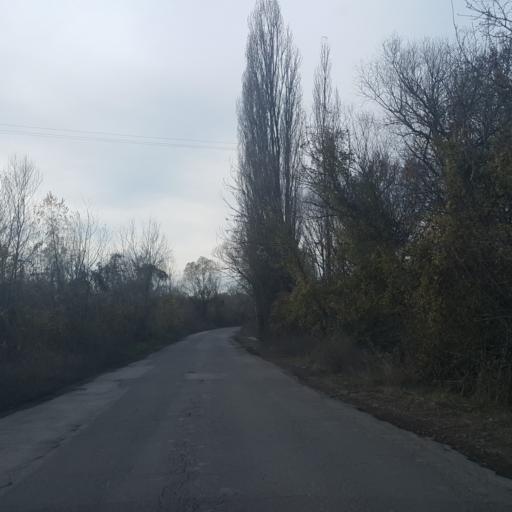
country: RS
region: Central Serbia
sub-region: Belgrade
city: Lazarevac
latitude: 44.4224
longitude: 20.2942
